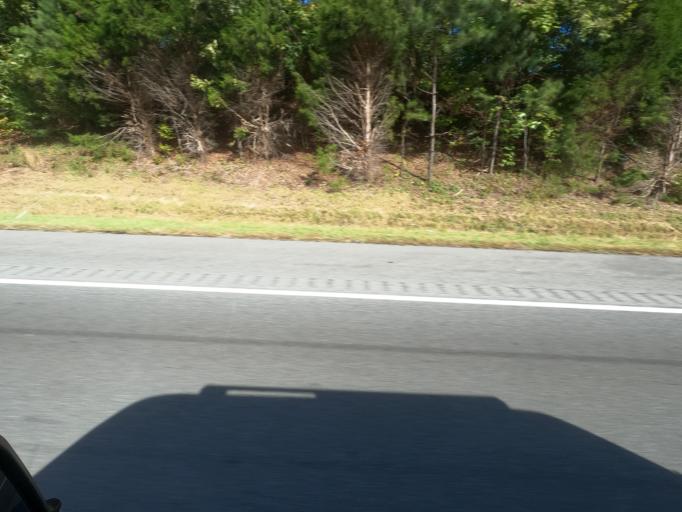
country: US
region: Tennessee
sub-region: Dickson County
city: Dickson
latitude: 35.9964
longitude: -87.4526
